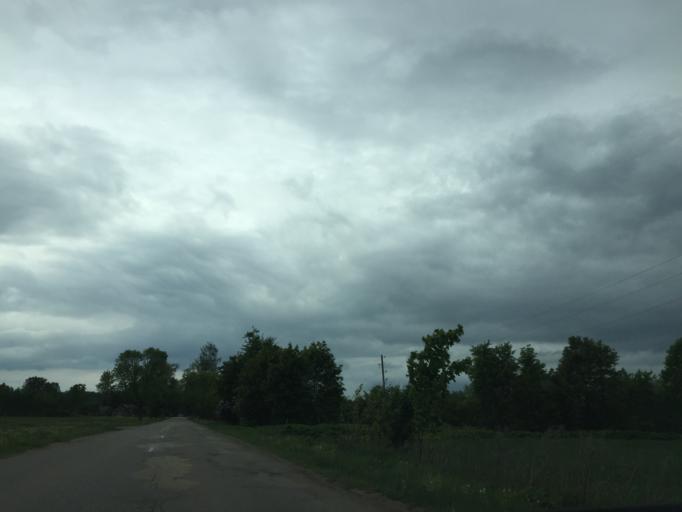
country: LV
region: Preilu Rajons
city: Preili
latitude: 56.0699
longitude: 26.7494
